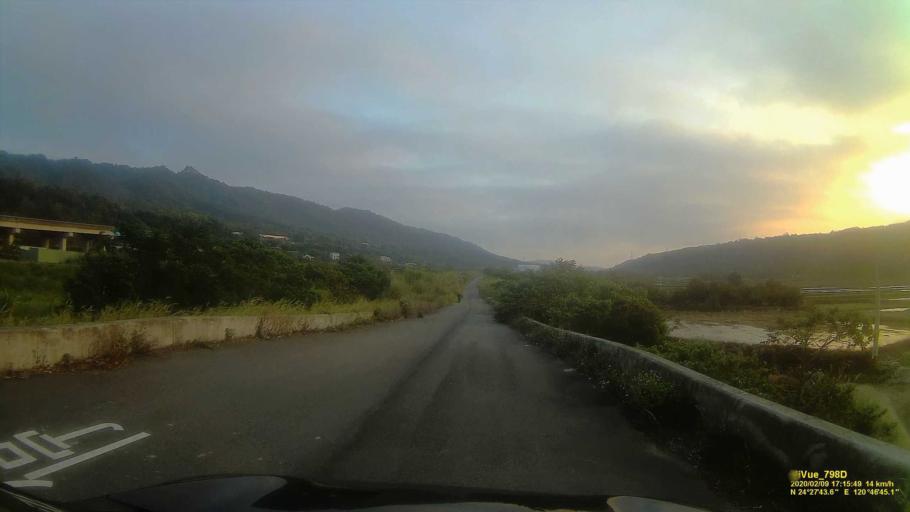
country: TW
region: Taiwan
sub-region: Miaoli
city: Miaoli
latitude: 24.4620
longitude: 120.7792
